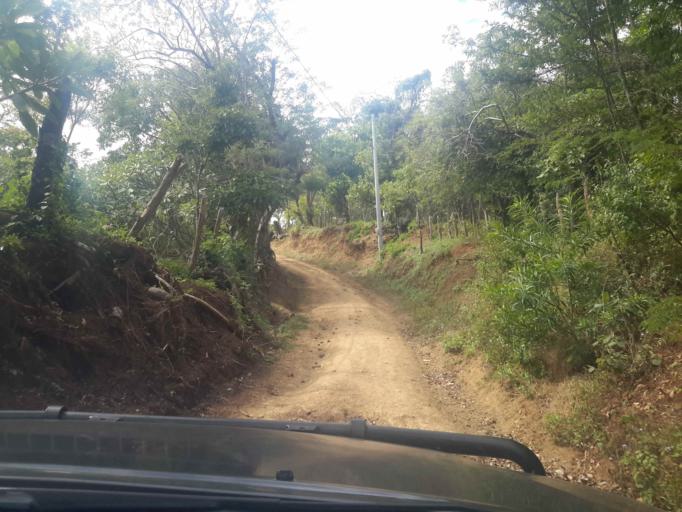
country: NI
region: Carazo
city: Santa Teresa
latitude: 11.6556
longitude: -86.1932
